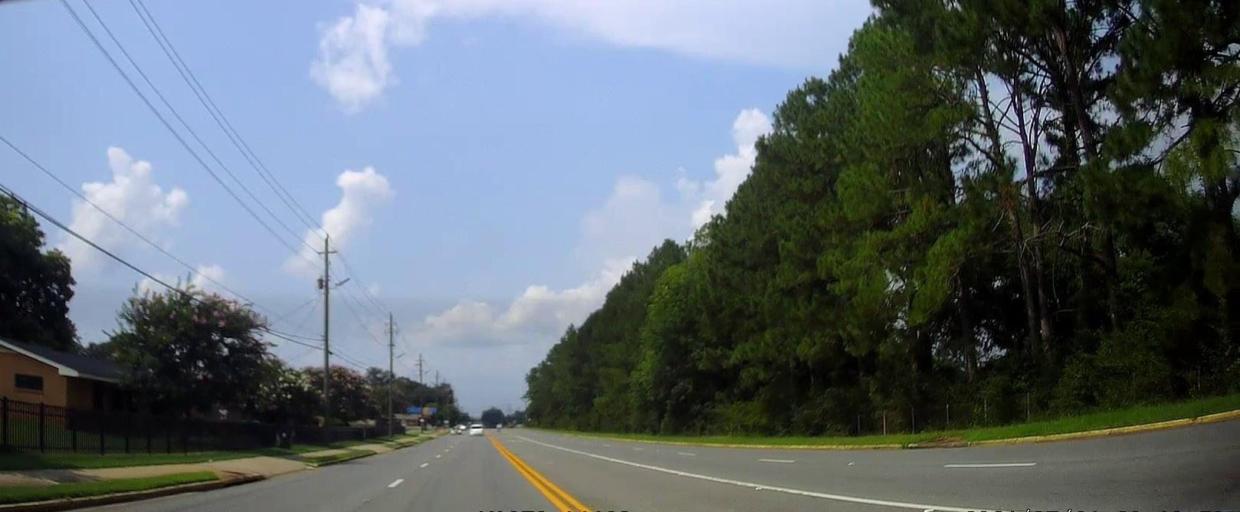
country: US
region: Georgia
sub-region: Houston County
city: Warner Robins
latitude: 32.6041
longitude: -83.6134
